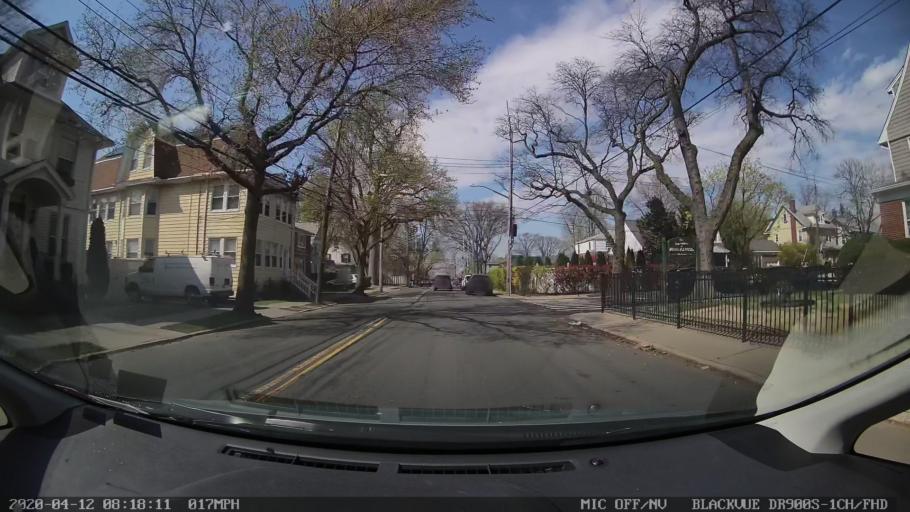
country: US
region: New York
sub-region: Richmond County
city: Bloomfield
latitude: 40.6173
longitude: -74.1312
